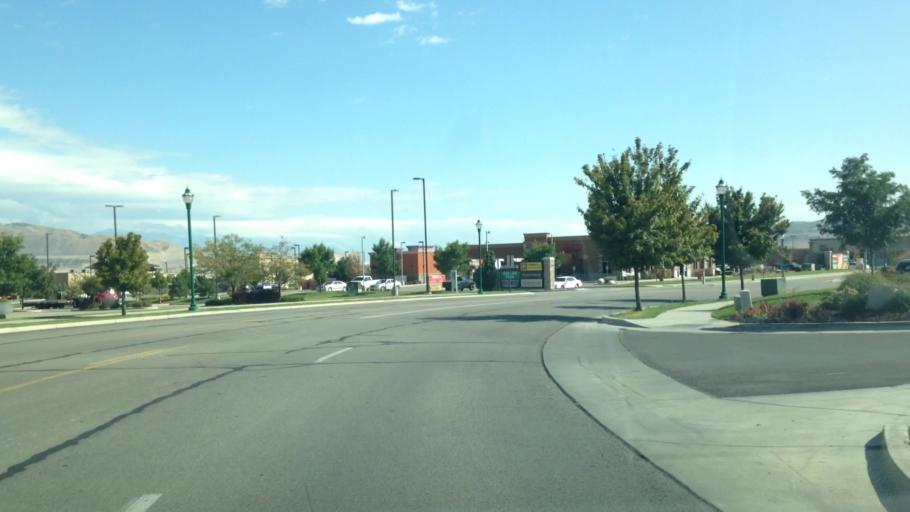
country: US
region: Utah
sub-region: Salt Lake County
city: Riverton
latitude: 40.5095
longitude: -111.9797
